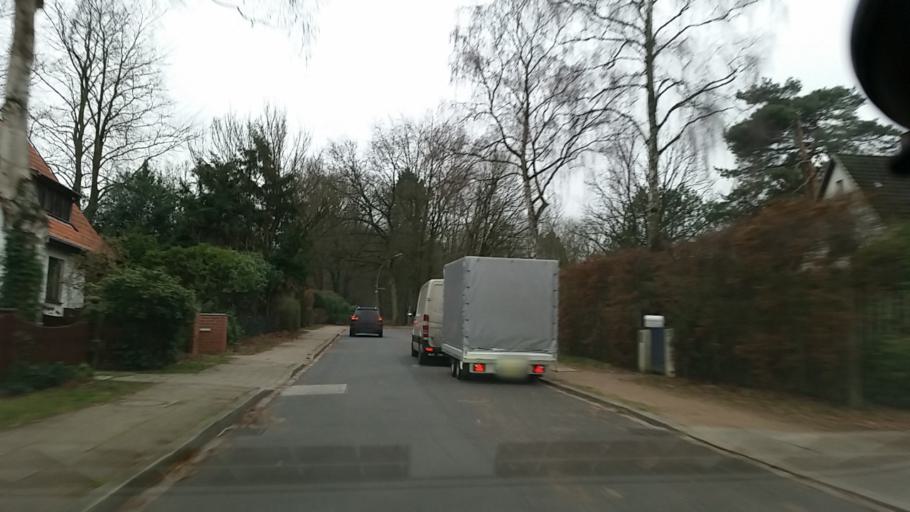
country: DE
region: Schleswig-Holstein
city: Rellingen
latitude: 53.5761
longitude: 9.7961
